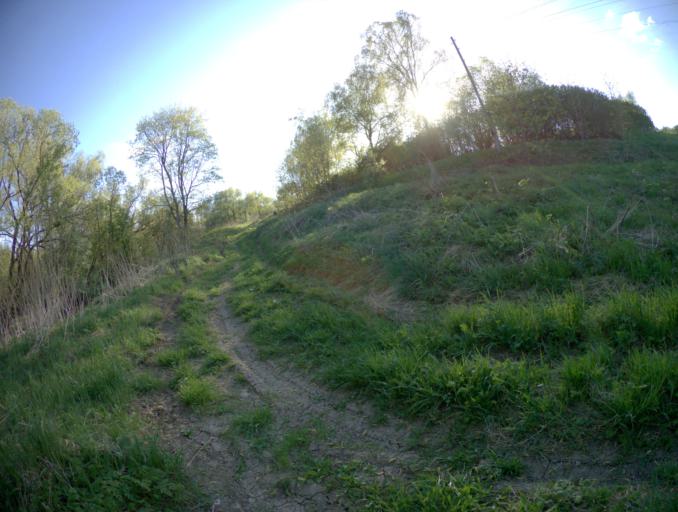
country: RU
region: Ivanovo
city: Gavrilov Posad
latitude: 56.3825
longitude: 40.1408
